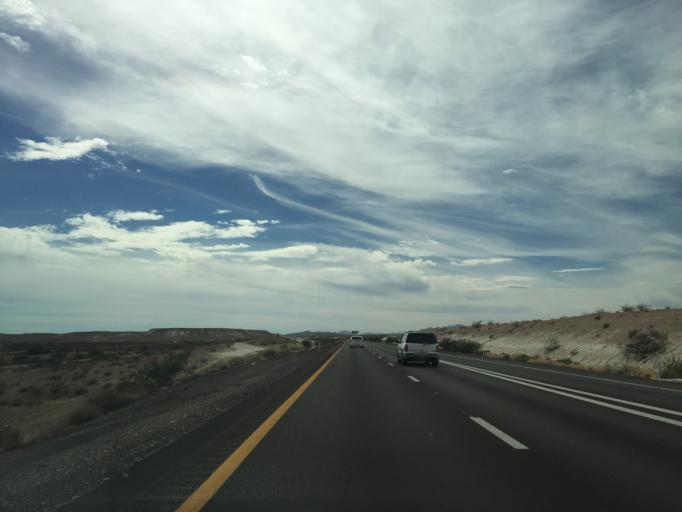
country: US
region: Nevada
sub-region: Clark County
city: Moapa Town
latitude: 36.5530
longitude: -114.6974
